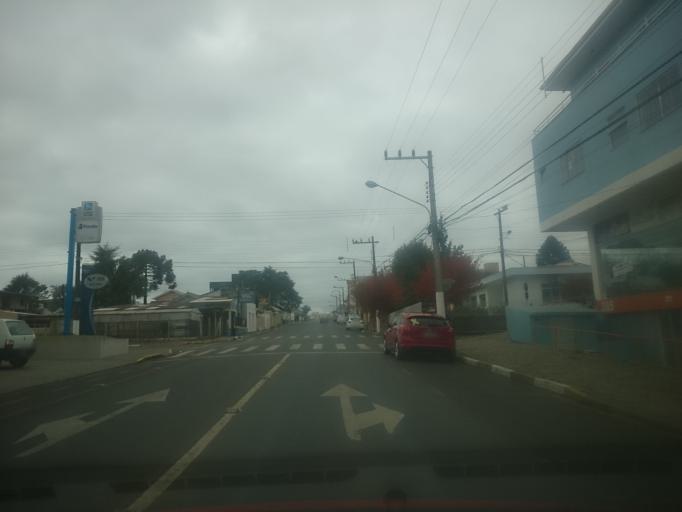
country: BR
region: Santa Catarina
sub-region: Lages
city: Lages
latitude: -27.8071
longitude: -50.3173
